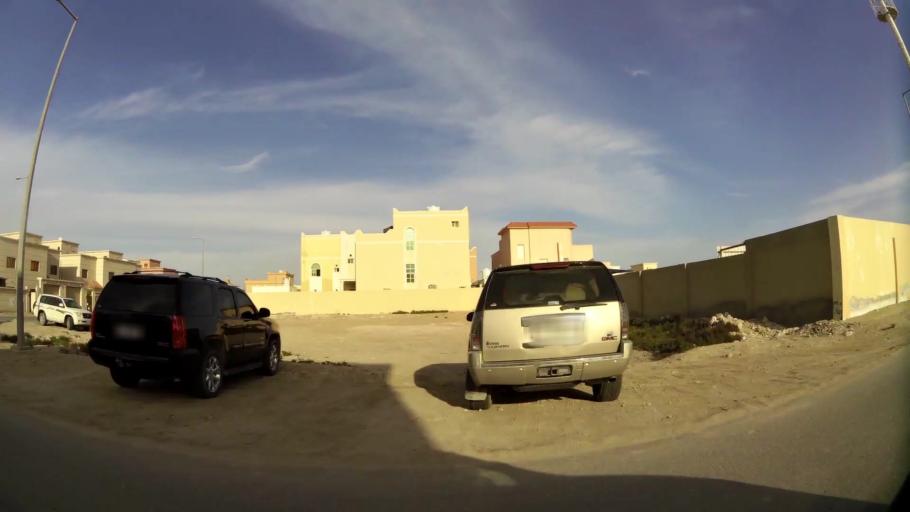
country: QA
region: Al Wakrah
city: Al Wakrah
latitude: 25.1421
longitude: 51.6139
